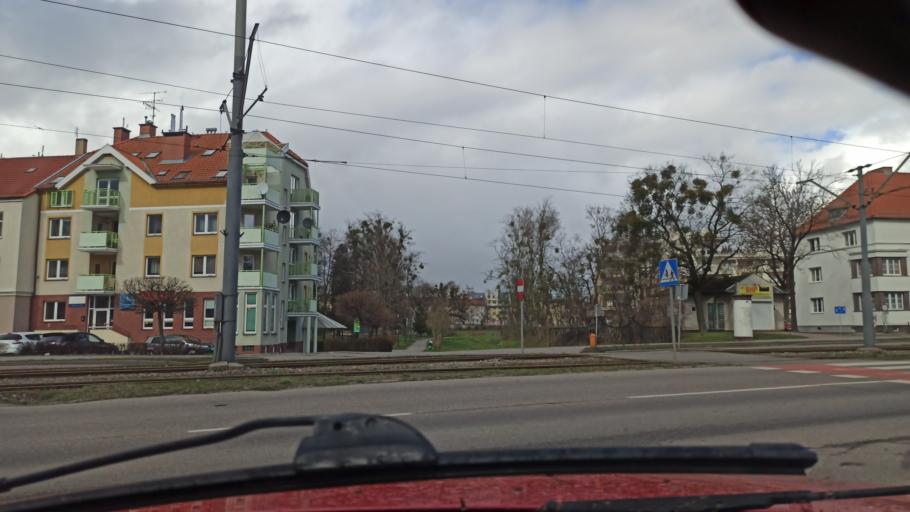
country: PL
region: Warmian-Masurian Voivodeship
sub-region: Powiat elblaski
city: Elblag
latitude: 54.1589
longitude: 19.4134
